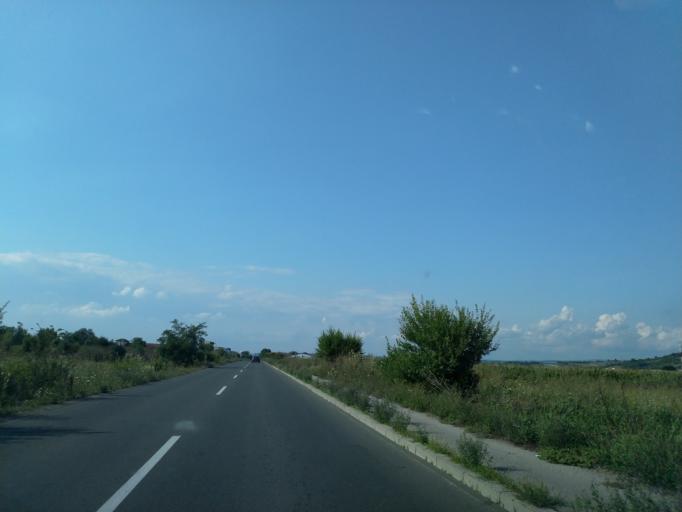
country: RS
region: Central Serbia
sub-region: Pomoravski Okrug
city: Paracin
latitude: 43.8232
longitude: 21.4182
